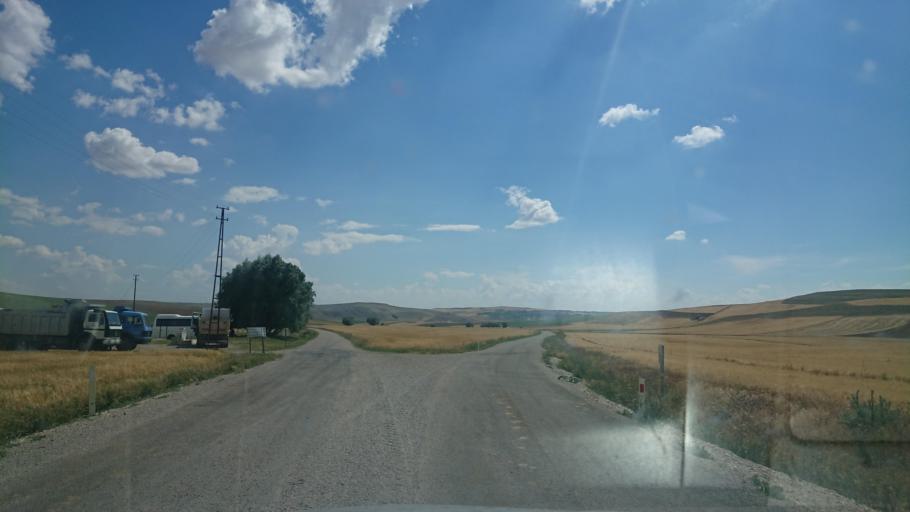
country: TR
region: Aksaray
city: Agacoren
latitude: 38.7995
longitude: 33.8246
